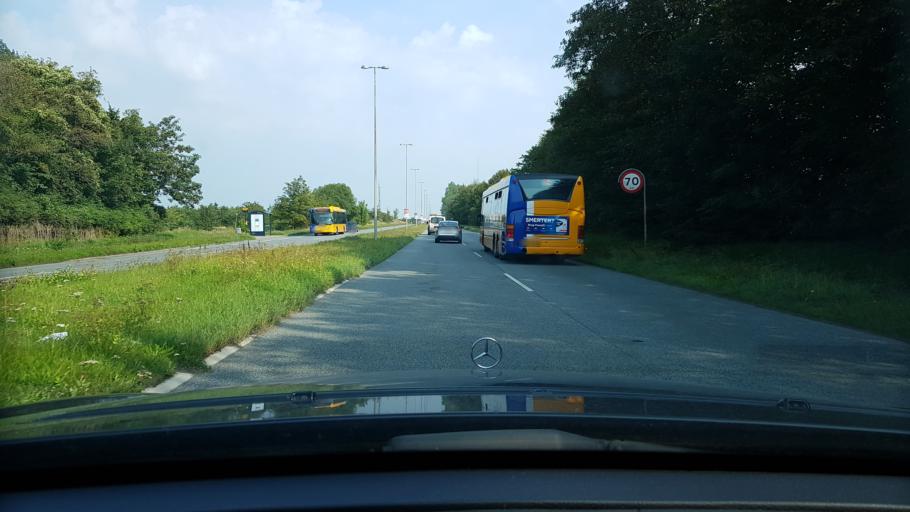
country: DK
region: North Denmark
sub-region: Alborg Kommune
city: Gistrup
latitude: 57.0303
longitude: 9.9783
